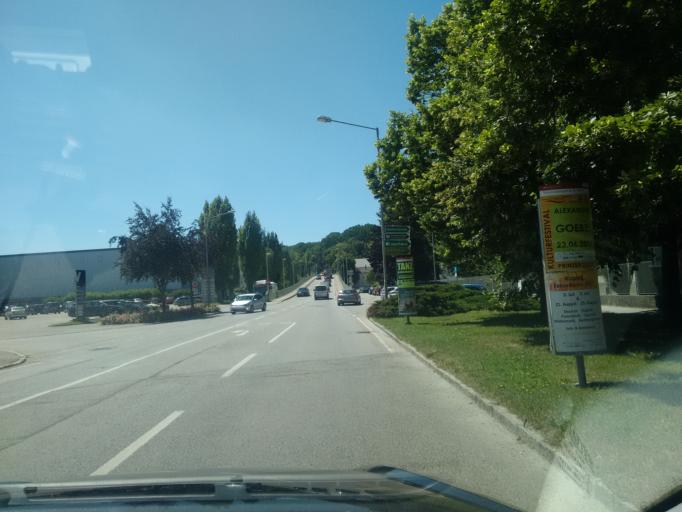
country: AT
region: Lower Austria
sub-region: Sankt Polten Stadt
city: Sankt Poelten
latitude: 48.2007
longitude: 15.6173
